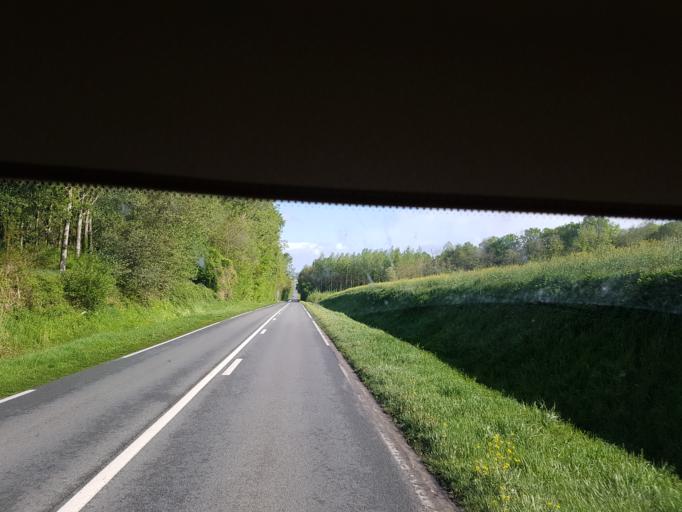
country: FR
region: Picardie
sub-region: Departement de l'Aisne
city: Sinceny
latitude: 49.6052
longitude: 3.2706
